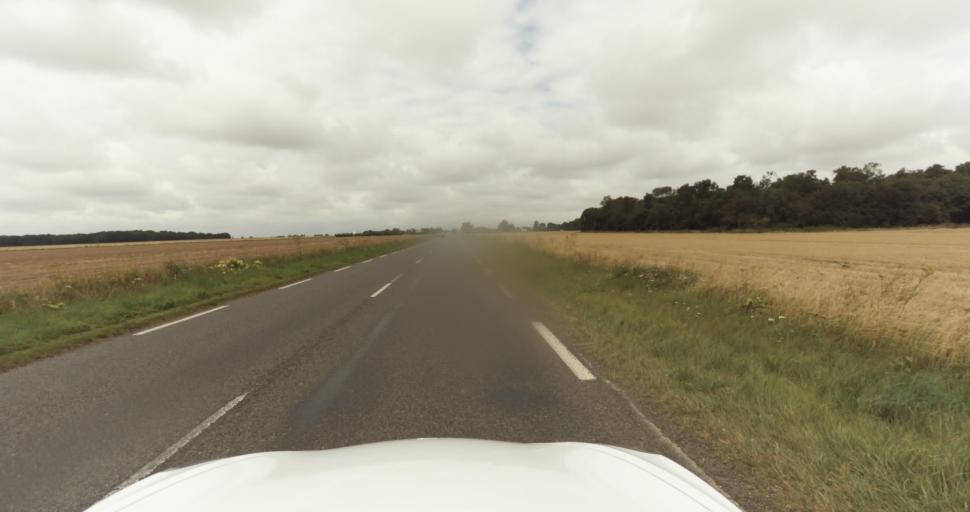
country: FR
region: Haute-Normandie
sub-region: Departement de l'Eure
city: Claville
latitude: 49.0392
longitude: 1.0284
